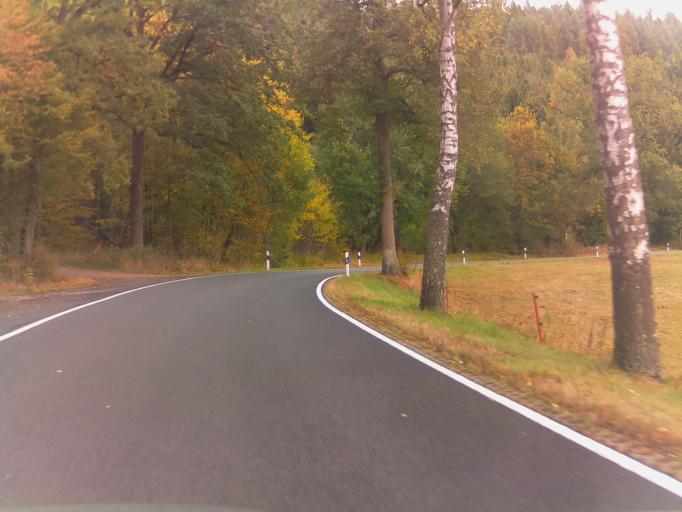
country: DE
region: Thuringia
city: Mehmels
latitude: 50.6477
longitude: 10.3471
